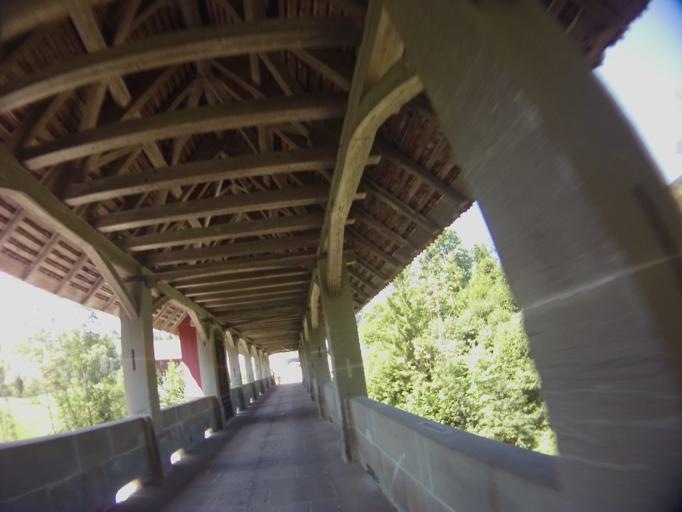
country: CH
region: Schwyz
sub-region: Bezirk Hoefe
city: Feusisberg
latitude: 47.1673
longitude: 8.7676
